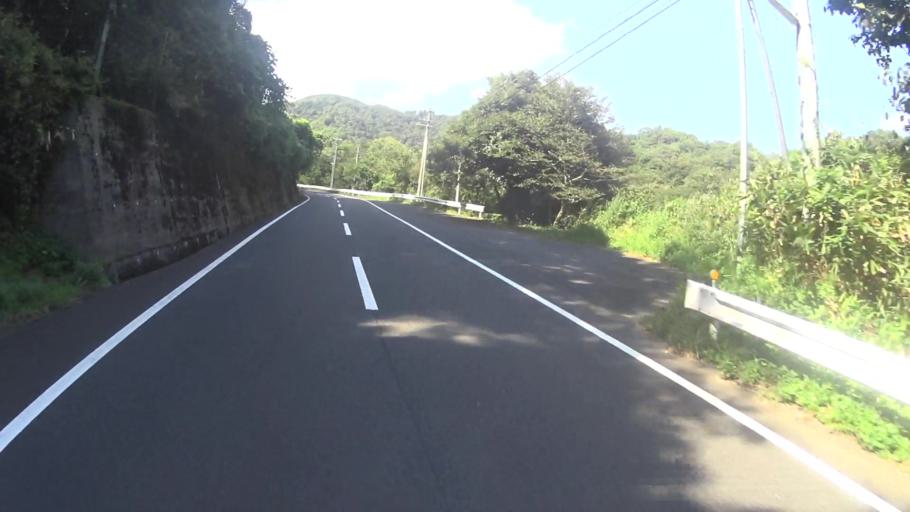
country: JP
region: Kyoto
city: Miyazu
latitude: 35.7055
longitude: 135.2816
